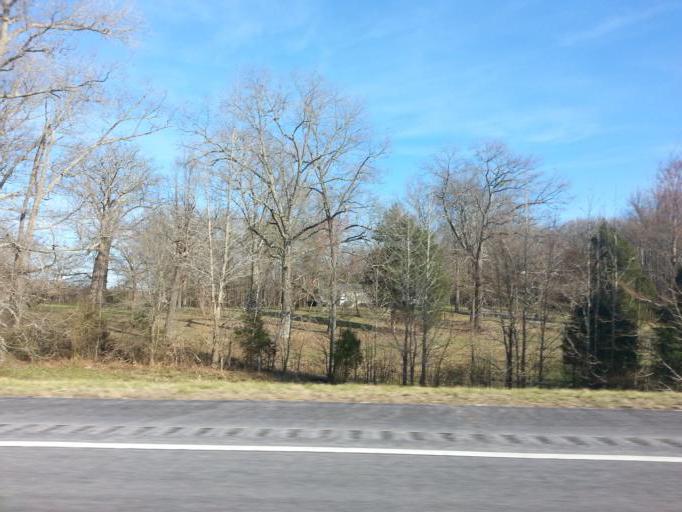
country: US
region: Tennessee
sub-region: Warren County
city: McMinnville
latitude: 35.7283
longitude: -85.6682
